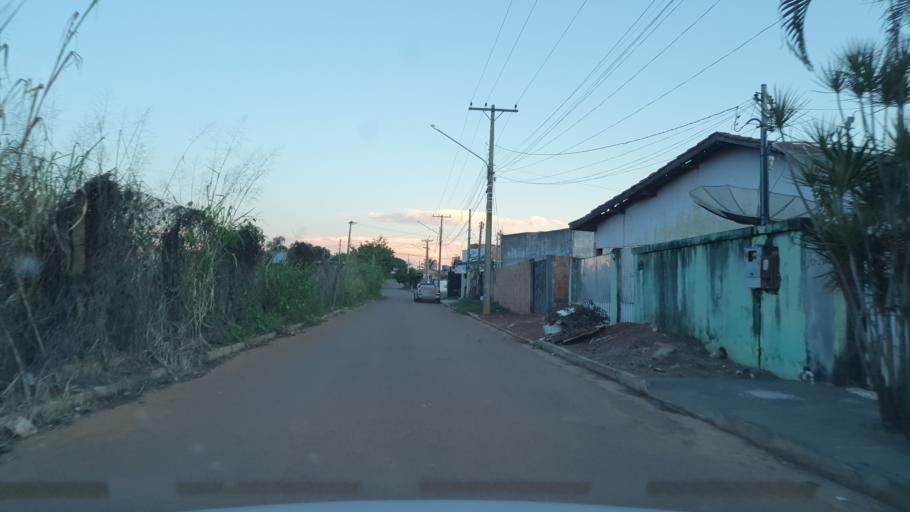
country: BR
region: Mato Grosso
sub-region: Pontes E Lacerda
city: Pontes e Lacerda
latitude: -15.2247
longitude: -59.3269
